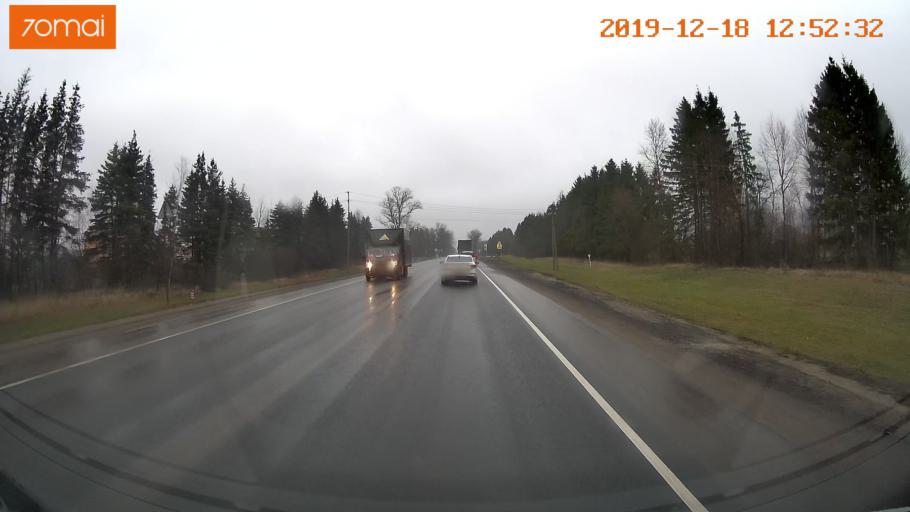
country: RU
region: Moskovskaya
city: Klin
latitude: 56.3122
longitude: 36.6883
